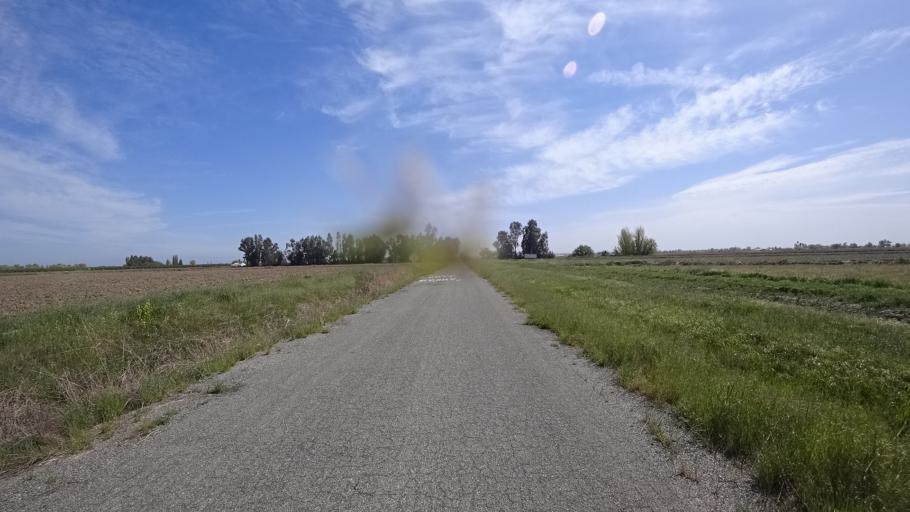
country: US
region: California
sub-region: Glenn County
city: Willows
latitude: 39.5948
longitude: -122.0639
